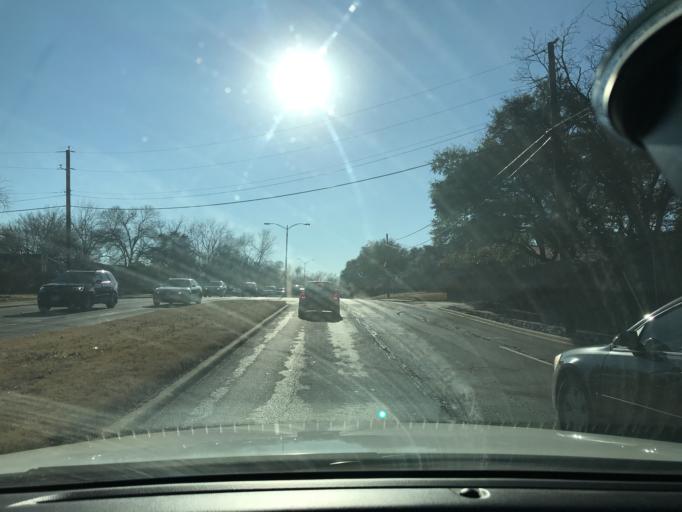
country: US
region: Texas
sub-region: Dallas County
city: Highland Park
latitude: 32.8391
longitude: -96.7458
